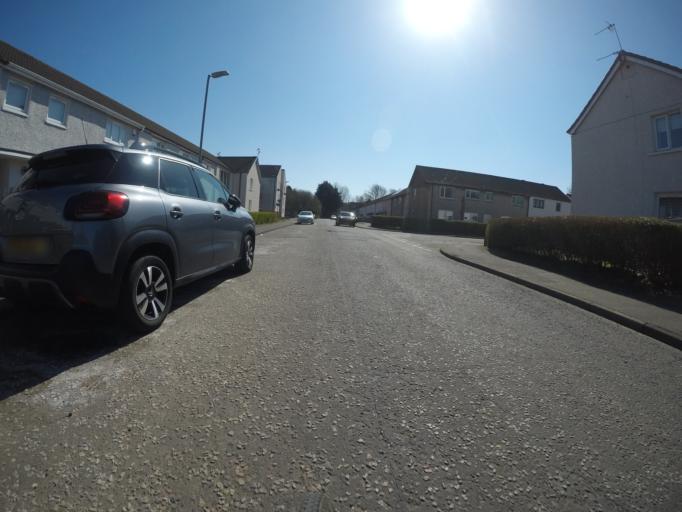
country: GB
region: Scotland
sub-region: North Ayrshire
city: Irvine
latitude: 55.6266
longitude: -4.6553
